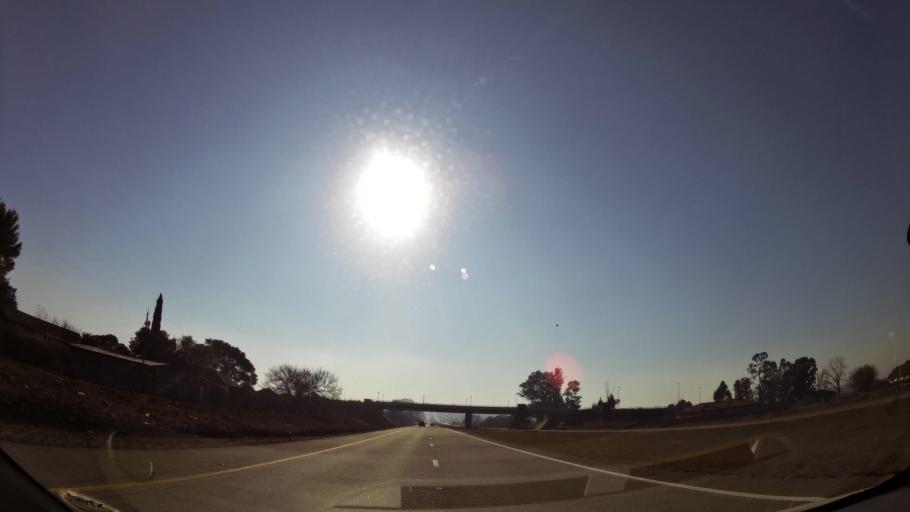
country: ZA
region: Mpumalanga
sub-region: Nkangala District Municipality
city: Witbank
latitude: -25.9257
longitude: 29.2227
